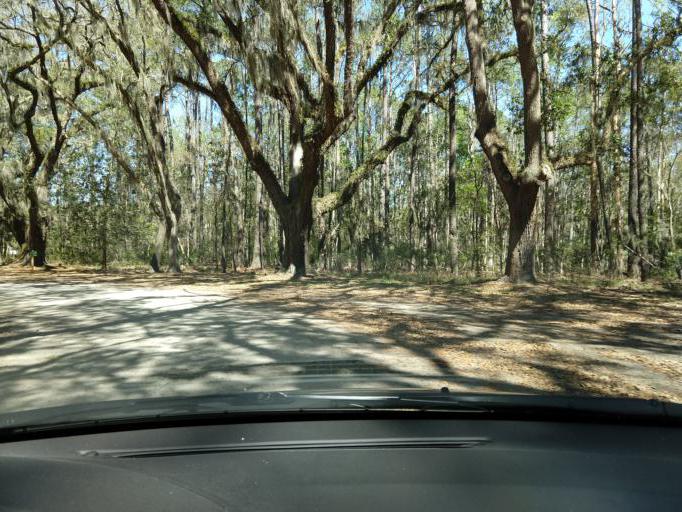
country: US
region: Georgia
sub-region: Chatham County
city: Isle of Hope
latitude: 31.9631
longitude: -81.0696
